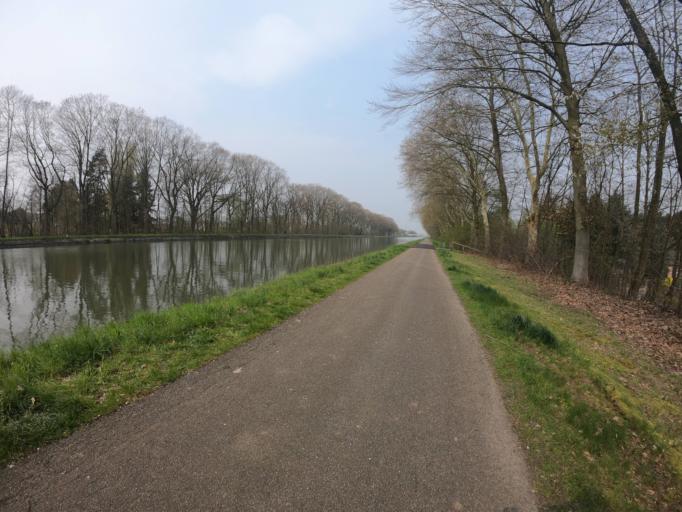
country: BE
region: Flanders
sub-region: Provincie Limburg
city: Maasmechelen
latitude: 51.0317
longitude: 5.7064
